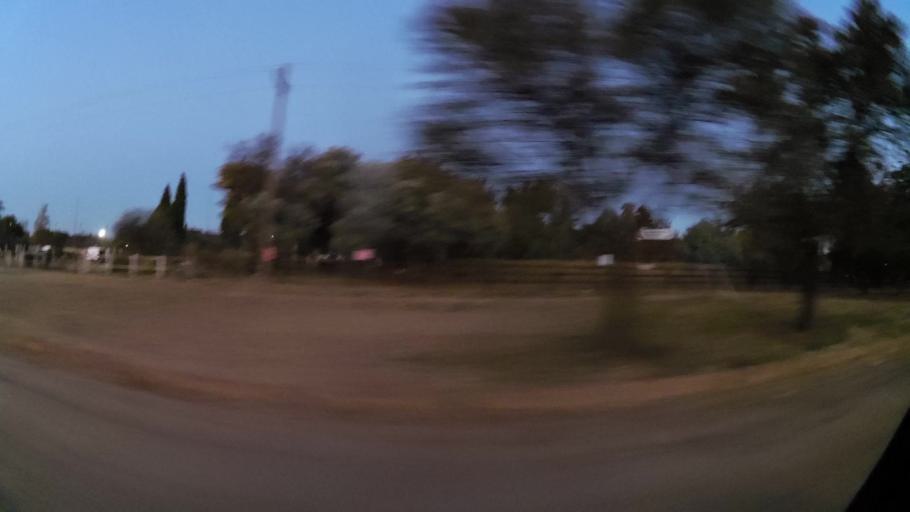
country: ZA
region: Gauteng
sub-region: City of Johannesburg Metropolitan Municipality
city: Midrand
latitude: -25.9528
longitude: 28.0877
